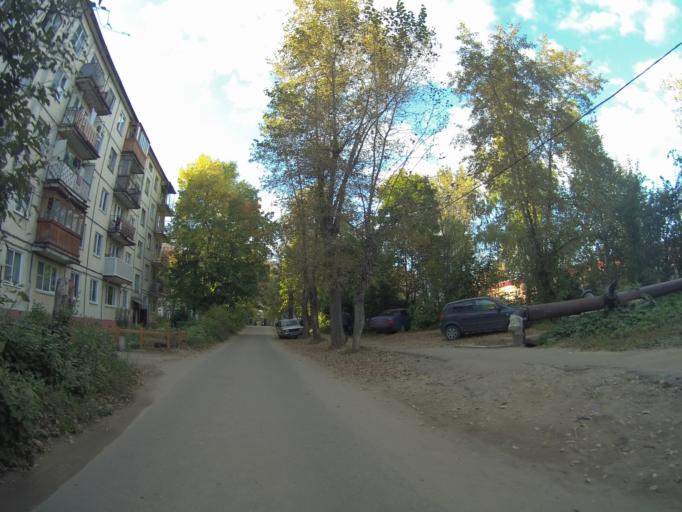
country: RU
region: Vladimir
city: Vladimir
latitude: 56.1143
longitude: 40.3490
